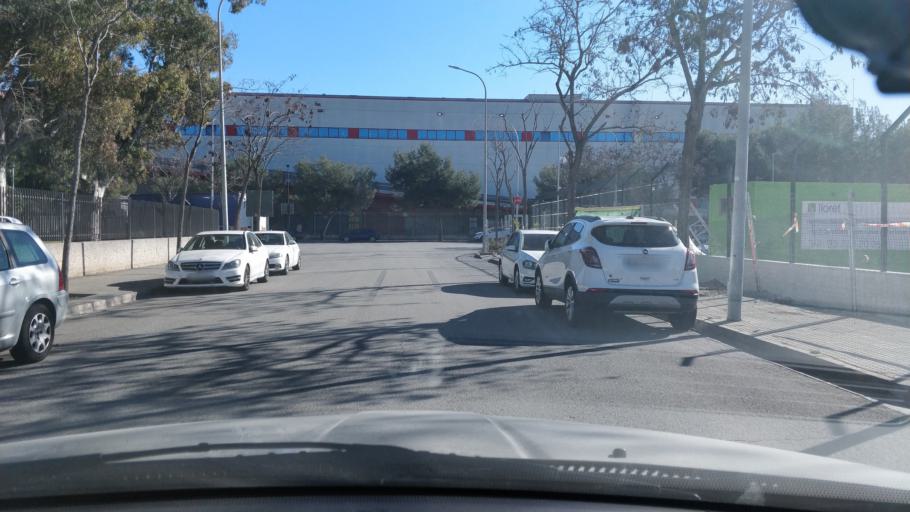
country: ES
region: Catalonia
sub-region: Provincia de Barcelona
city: El Prat de Llobregat
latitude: 41.3207
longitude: 2.0793
